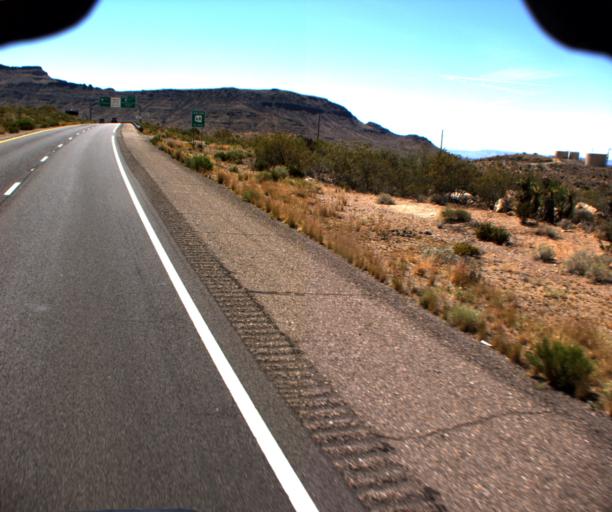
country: US
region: Arizona
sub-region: Mohave County
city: Golden Valley
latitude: 35.2319
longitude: -114.1373
